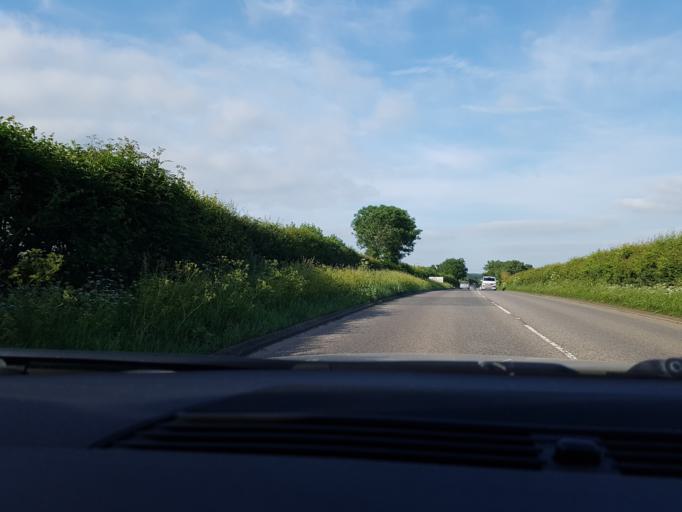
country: GB
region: England
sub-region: Buckinghamshire
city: Buckingham
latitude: 52.0052
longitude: -0.9639
